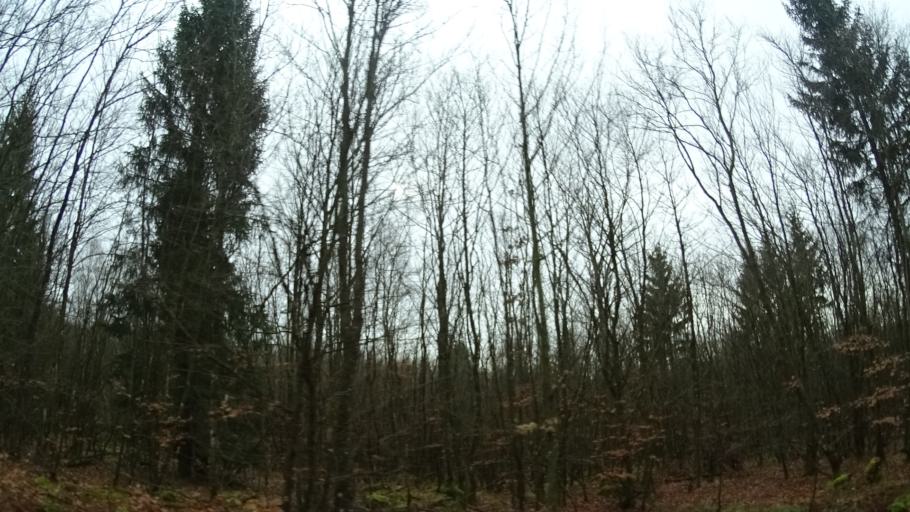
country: DE
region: Rheinland-Pfalz
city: Ippenschied
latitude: 49.8936
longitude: 7.6208
